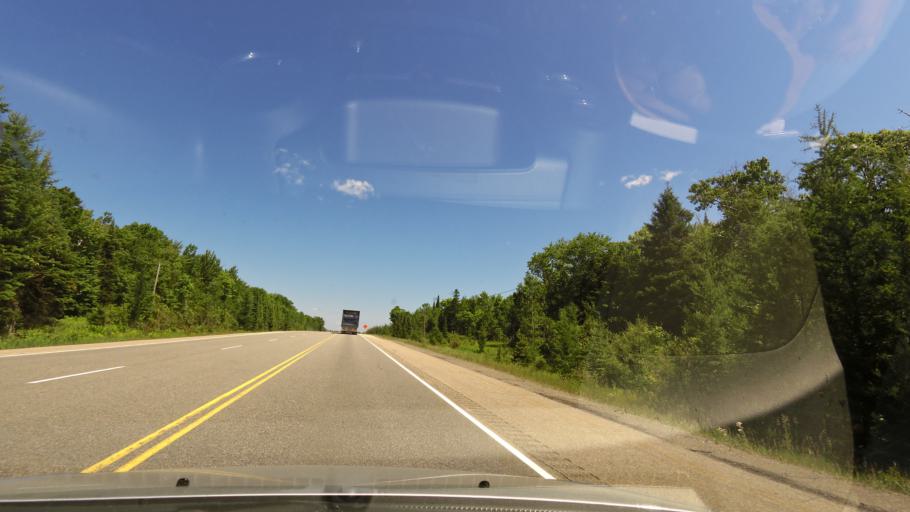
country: CA
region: Ontario
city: Greater Sudbury
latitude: 45.8801
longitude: -80.5683
